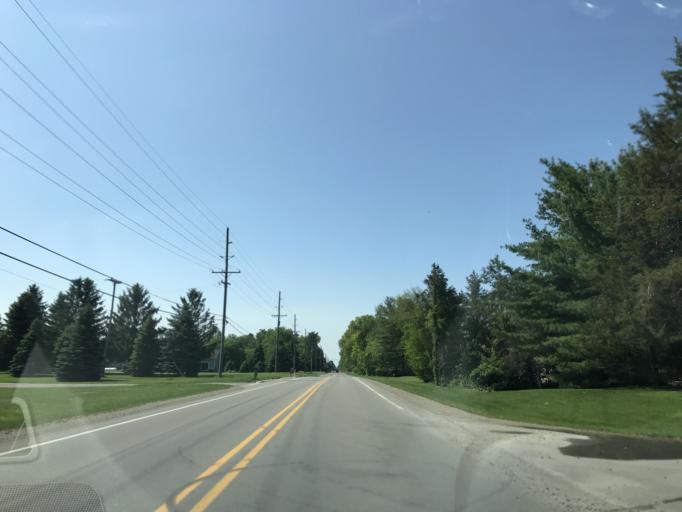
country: US
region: Michigan
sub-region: Oakland County
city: South Lyon
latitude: 42.4688
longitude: -83.6970
